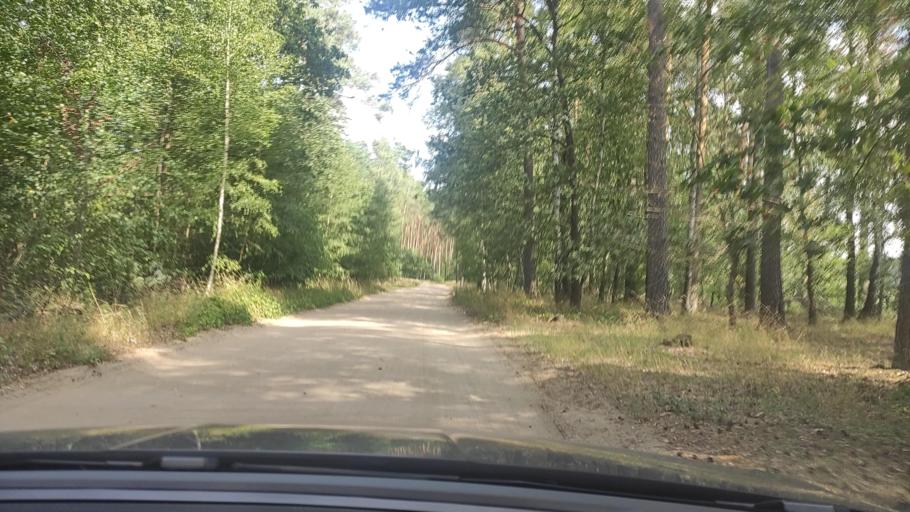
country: PL
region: Greater Poland Voivodeship
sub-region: Powiat poznanski
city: Pobiedziska
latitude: 52.4962
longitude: 17.2010
